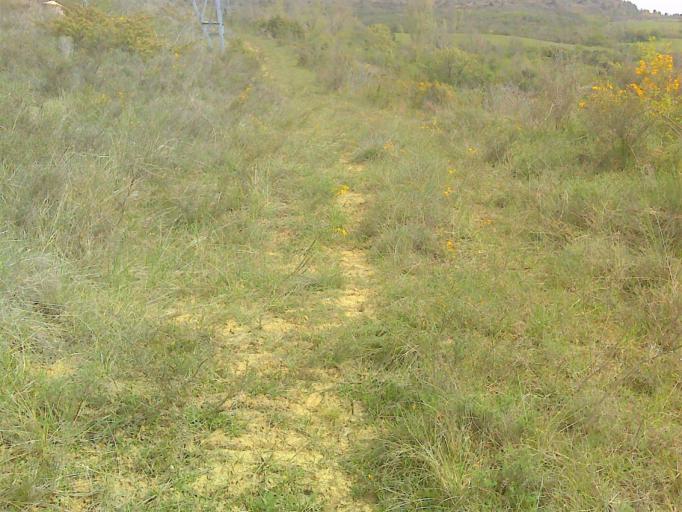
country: FR
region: Languedoc-Roussillon
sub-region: Departement de l'Aude
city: Esperaza
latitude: 42.9450
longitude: 2.2064
